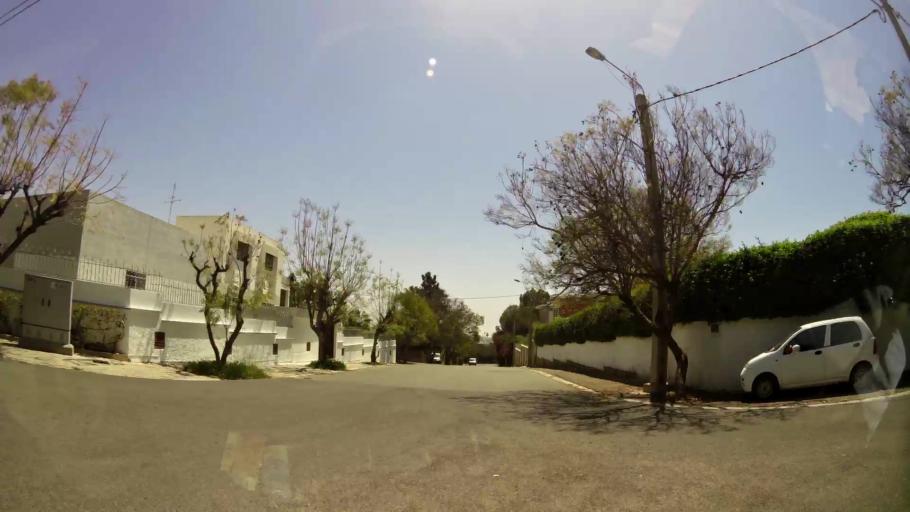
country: MA
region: Souss-Massa-Draa
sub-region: Agadir-Ida-ou-Tnan
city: Agadir
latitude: 30.4291
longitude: -9.5970
